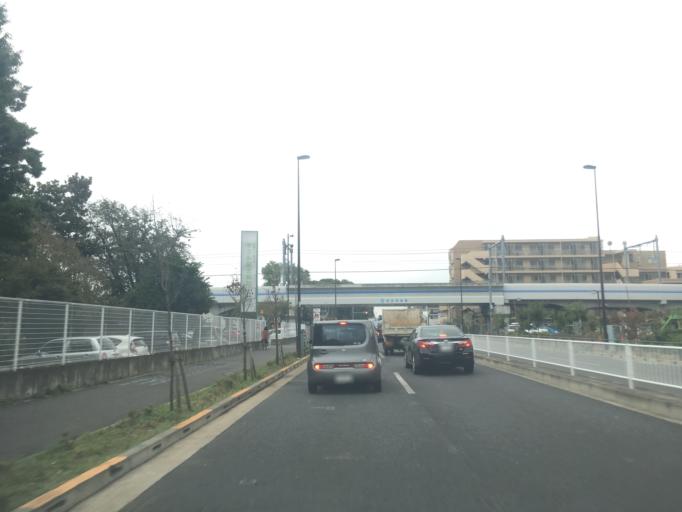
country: JP
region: Tokyo
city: Higashimurayama-shi
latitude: 35.7429
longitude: 139.4668
